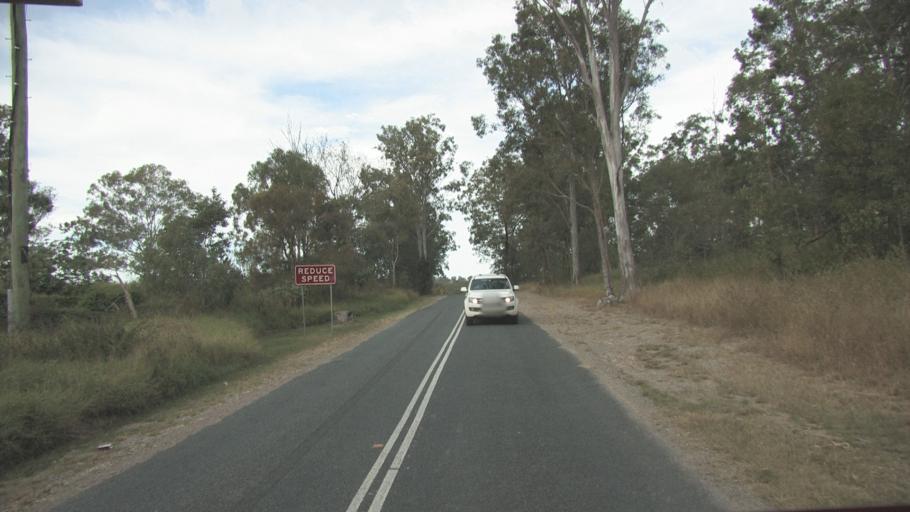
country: AU
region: Queensland
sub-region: Logan
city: Beenleigh
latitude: -27.7154
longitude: 153.1723
